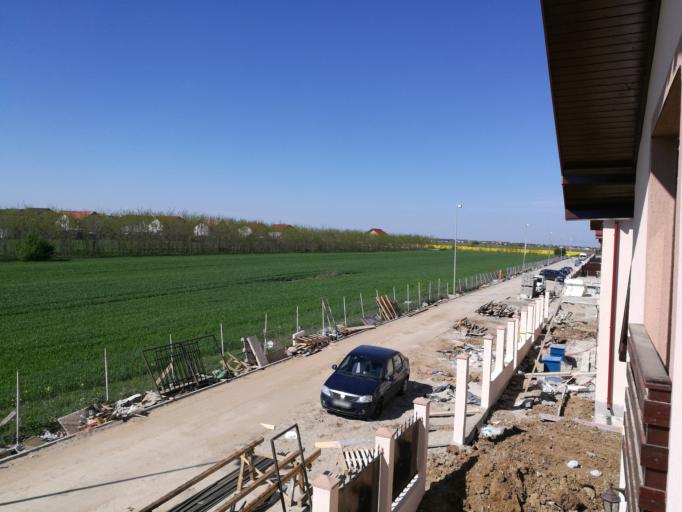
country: RO
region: Ilfov
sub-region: Comuna Vidra
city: Vidra
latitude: 44.2775
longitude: 26.1834
